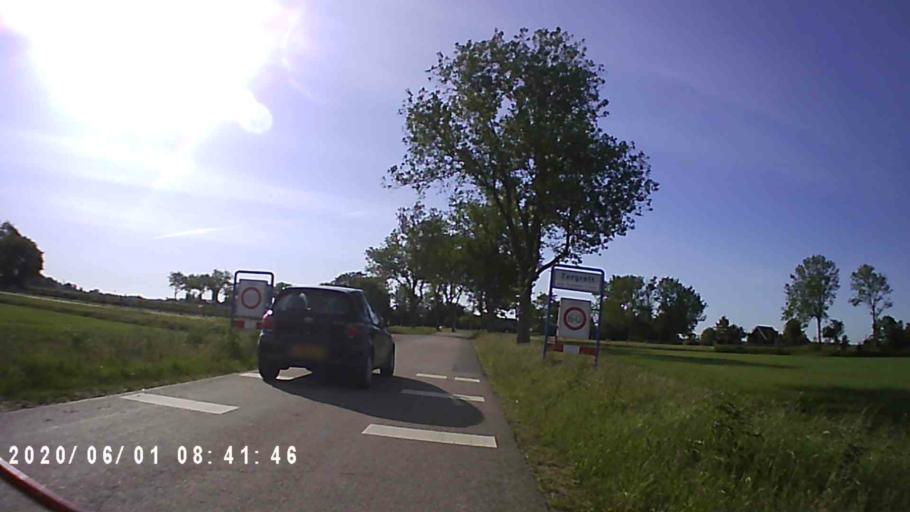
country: NL
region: Friesland
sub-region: Gemeente Ferwerderadiel
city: Burdaard
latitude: 53.2868
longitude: 5.8458
